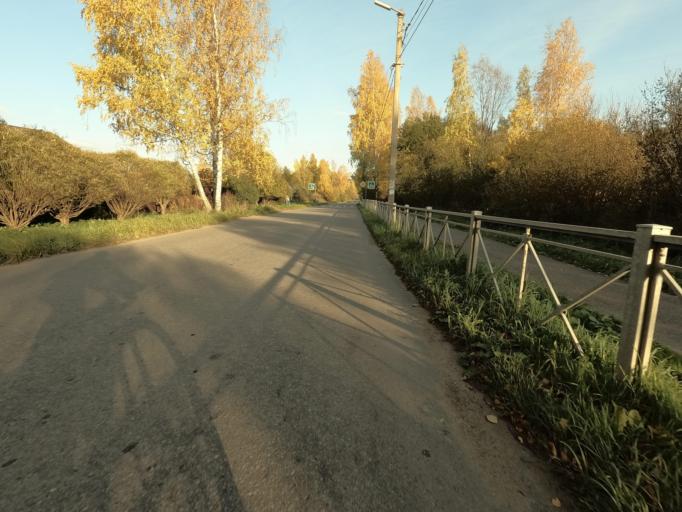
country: RU
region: Leningrad
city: Mga
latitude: 59.7579
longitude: 31.0477
